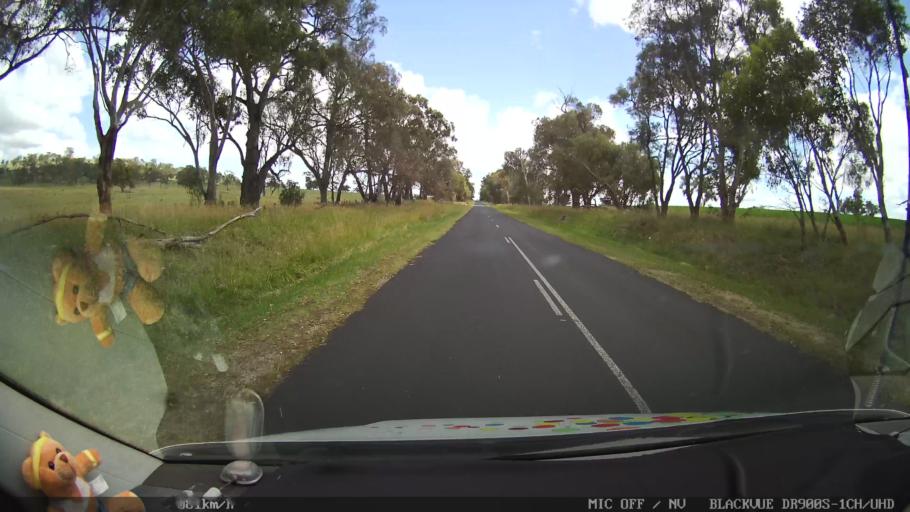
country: AU
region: New South Wales
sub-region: Glen Innes Severn
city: Glen Innes
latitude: -29.4833
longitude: 151.6842
